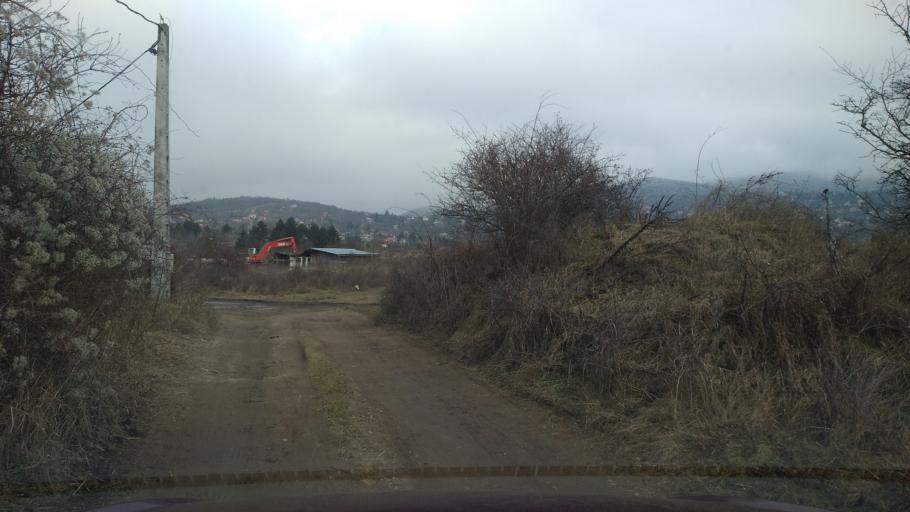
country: HU
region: Pest
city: Szentendre
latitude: 47.6911
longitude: 19.0393
